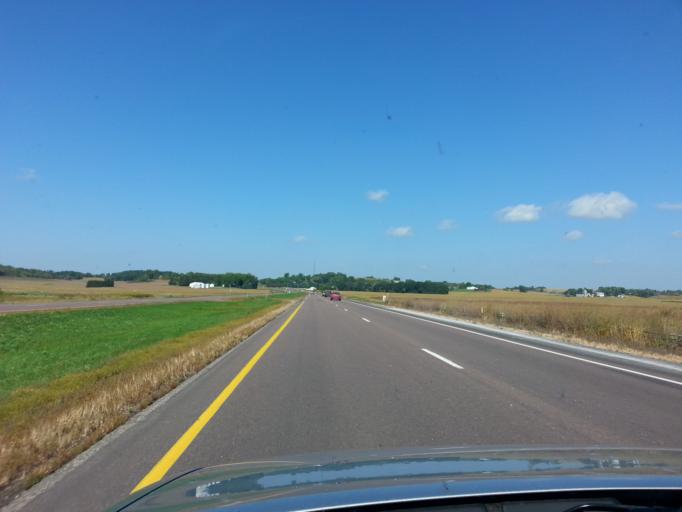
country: US
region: Minnesota
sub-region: Goodhue County
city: Cannon Falls
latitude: 44.5569
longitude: -92.9490
